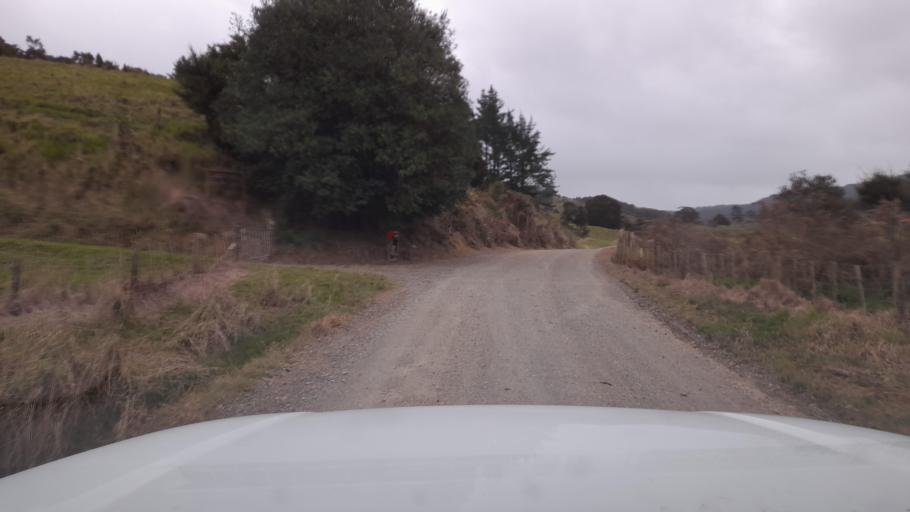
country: NZ
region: Northland
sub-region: Far North District
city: Paihia
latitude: -35.3420
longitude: 174.2328
